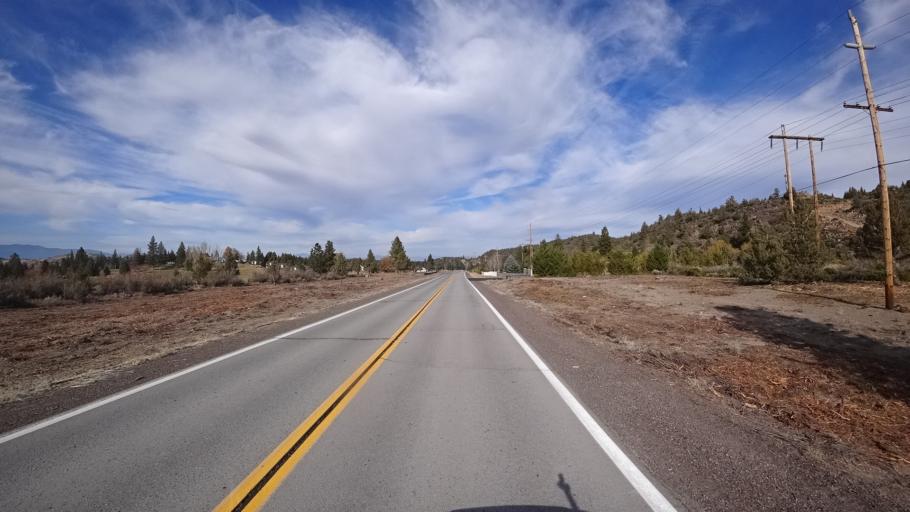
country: US
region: California
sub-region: Siskiyou County
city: Weed
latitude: 41.5070
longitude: -122.3639
